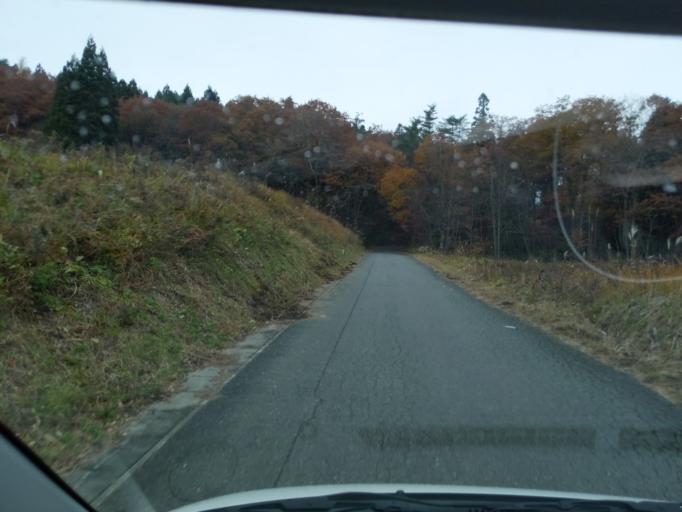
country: JP
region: Iwate
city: Ichinoseki
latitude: 38.9800
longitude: 141.0021
